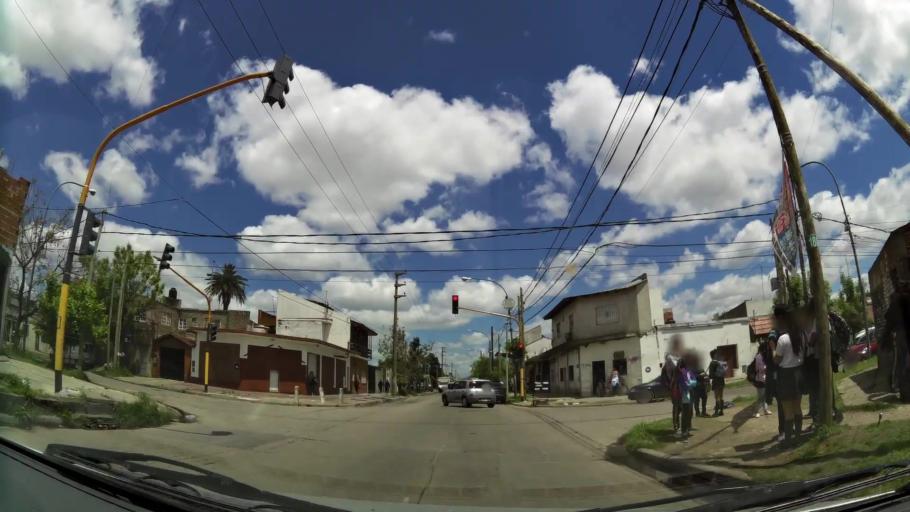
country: AR
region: Buenos Aires
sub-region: Partido de Lanus
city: Lanus
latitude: -34.7030
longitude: -58.4293
